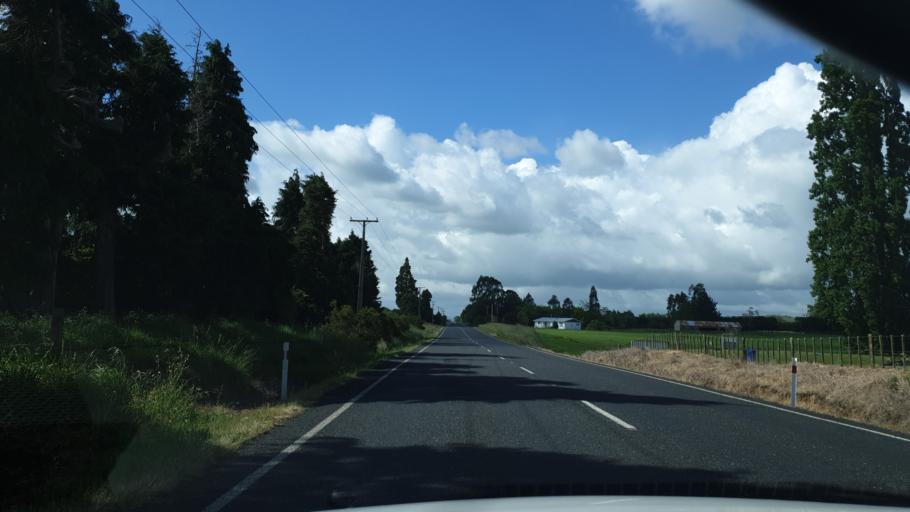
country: NZ
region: Waikato
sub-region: Hauraki District
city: Paeroa
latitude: -37.5077
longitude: 175.4954
